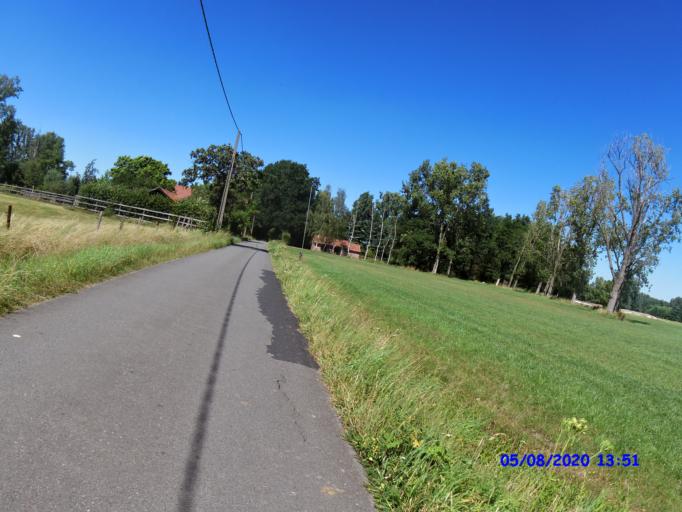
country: BE
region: Flanders
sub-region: Provincie Antwerpen
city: Hoogstraten
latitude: 51.3810
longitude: 4.7866
